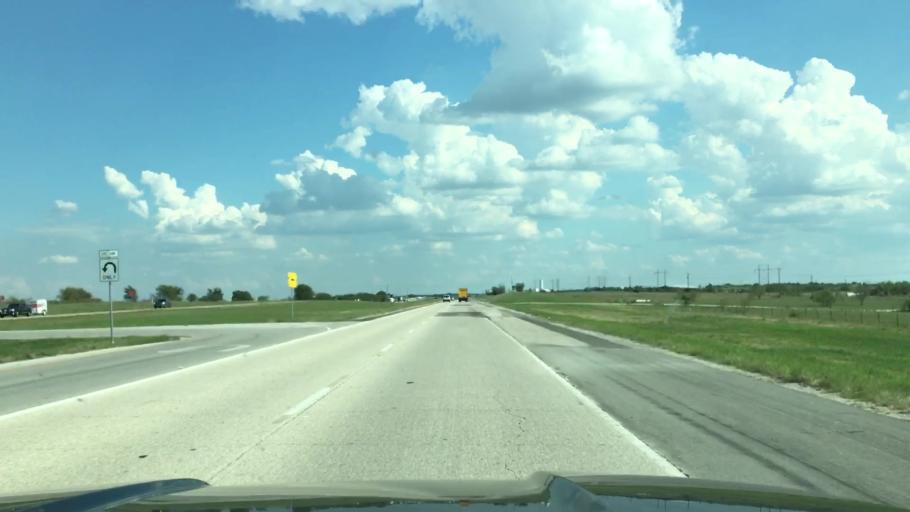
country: US
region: Texas
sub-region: Wise County
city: Decatur
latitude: 33.1872
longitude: -97.5542
